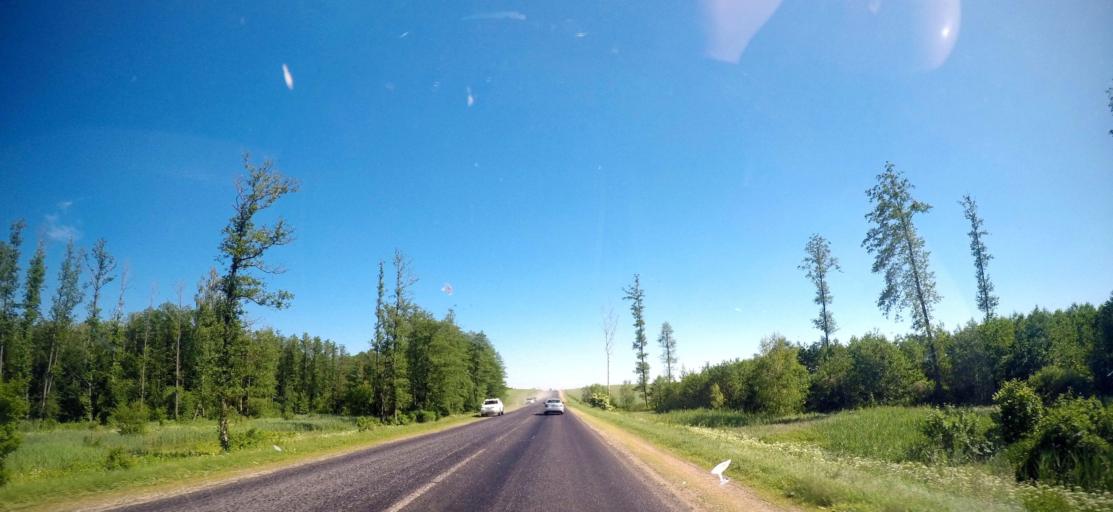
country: BY
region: Grodnenskaya
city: Vyalikaya Byerastavitsa
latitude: 53.2178
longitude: 23.9985
